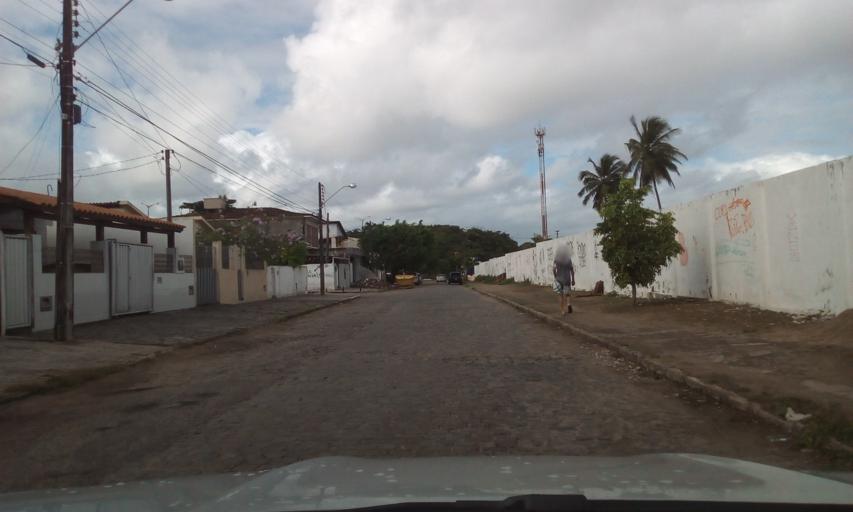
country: BR
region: Paraiba
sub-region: Joao Pessoa
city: Joao Pessoa
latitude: -7.1357
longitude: -34.8506
